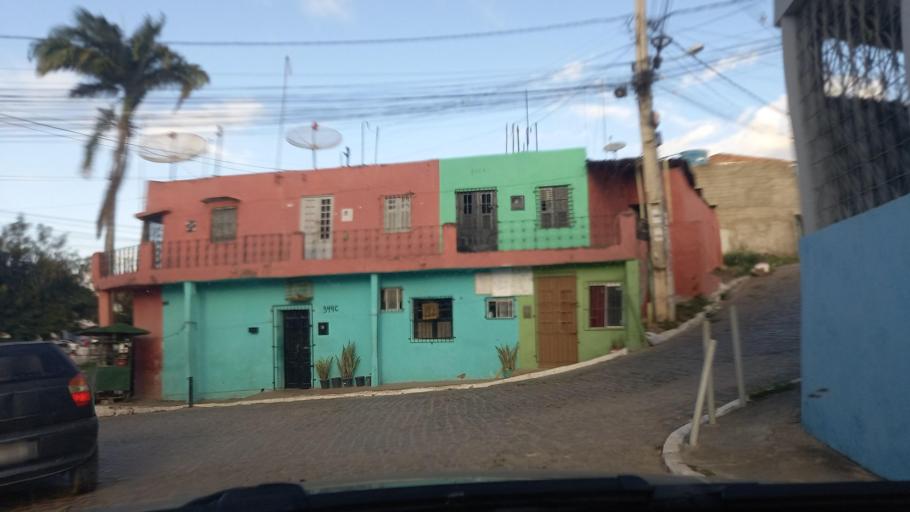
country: BR
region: Pernambuco
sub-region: Vitoria De Santo Antao
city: Vitoria de Santo Antao
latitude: -8.1238
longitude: -35.2963
